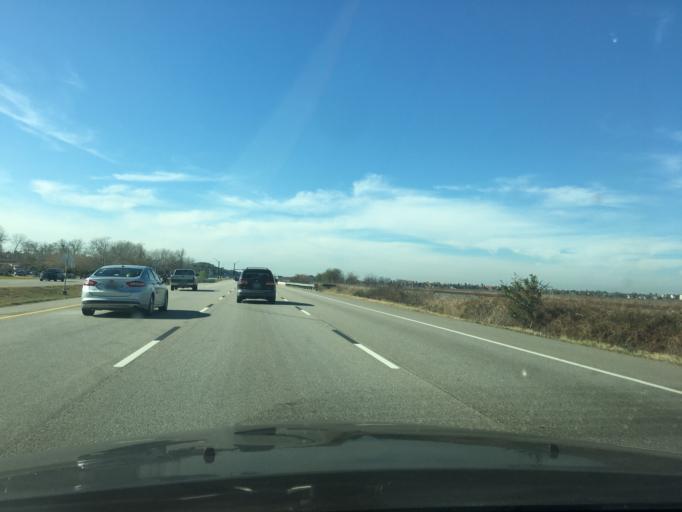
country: US
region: Texas
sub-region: Fort Bend County
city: New Territory
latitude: 29.6078
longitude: -95.6623
